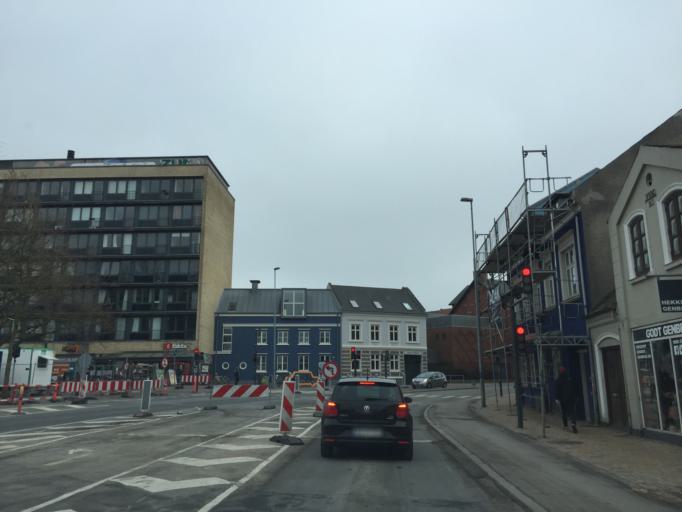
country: DK
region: South Denmark
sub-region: Odense Kommune
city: Odense
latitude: 55.3927
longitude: 10.3965
